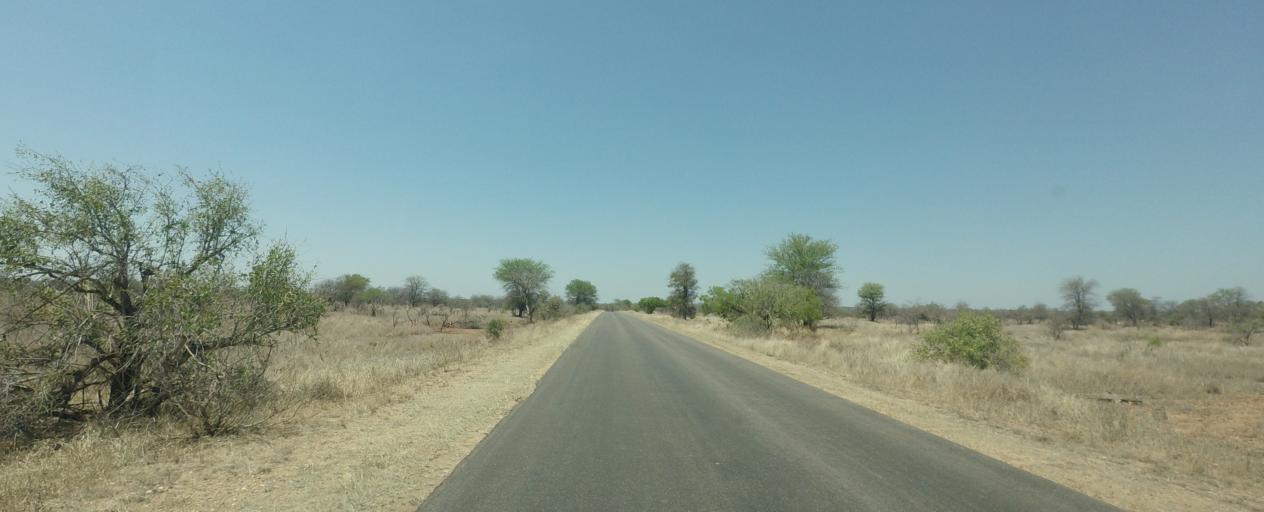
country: ZA
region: Limpopo
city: Thulamahashi
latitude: -24.4728
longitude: 31.4206
